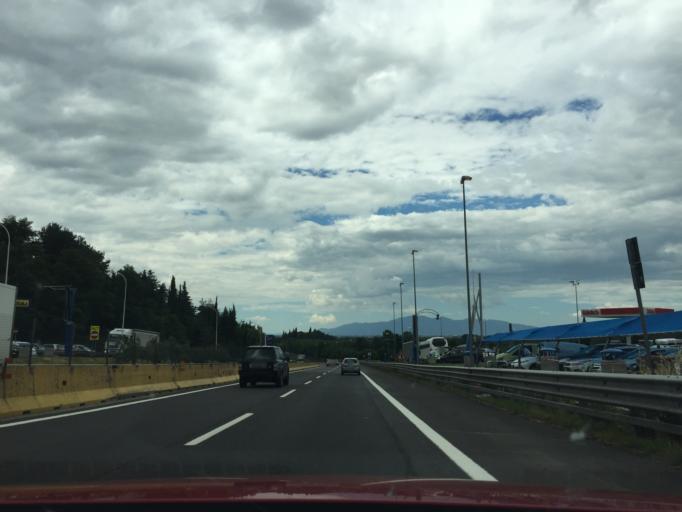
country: IT
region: Tuscany
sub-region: Provincia di Pistoia
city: Serravalle Pistoiese
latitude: 43.8913
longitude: 10.8251
